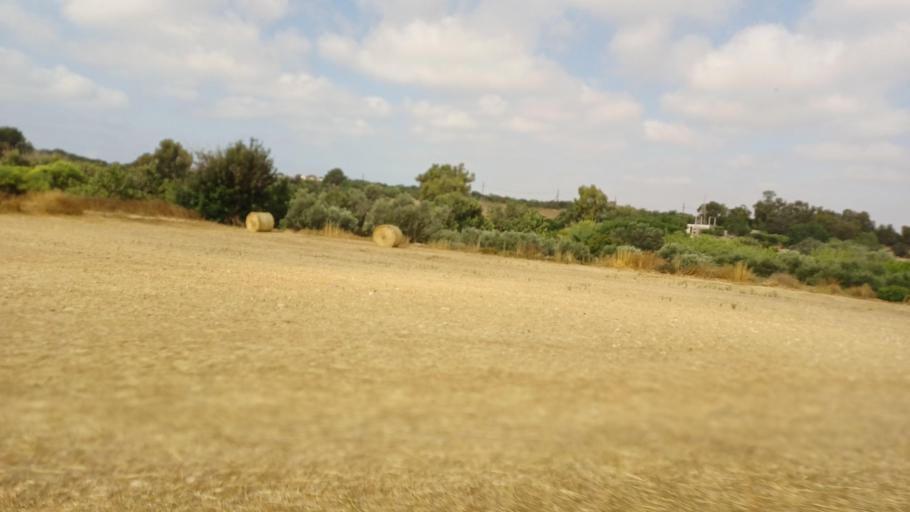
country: CY
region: Ammochostos
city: Ayia Napa
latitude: 35.0136
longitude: 34.0075
